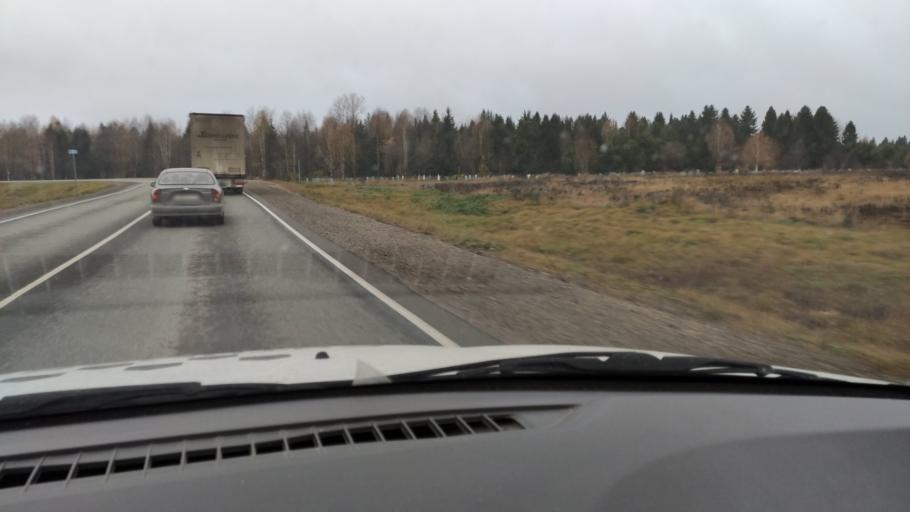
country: RU
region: Kirov
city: Omutninsk
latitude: 58.6932
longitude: 52.2007
